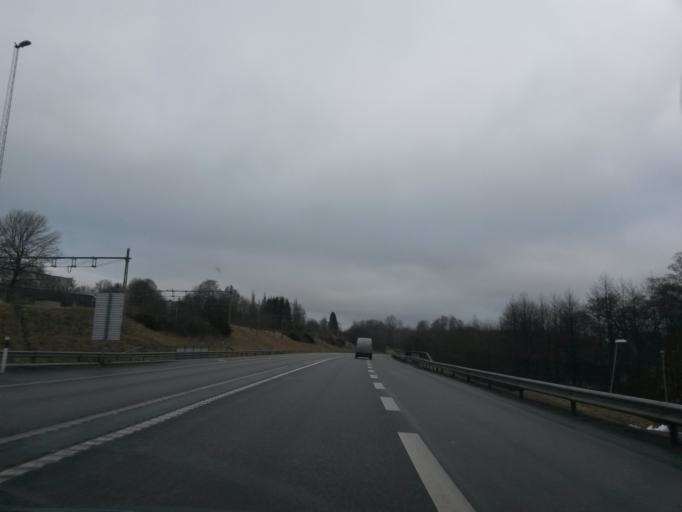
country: SE
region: Vaestra Goetaland
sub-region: Marks Kommun
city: Kinna
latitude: 57.5054
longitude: 12.6983
